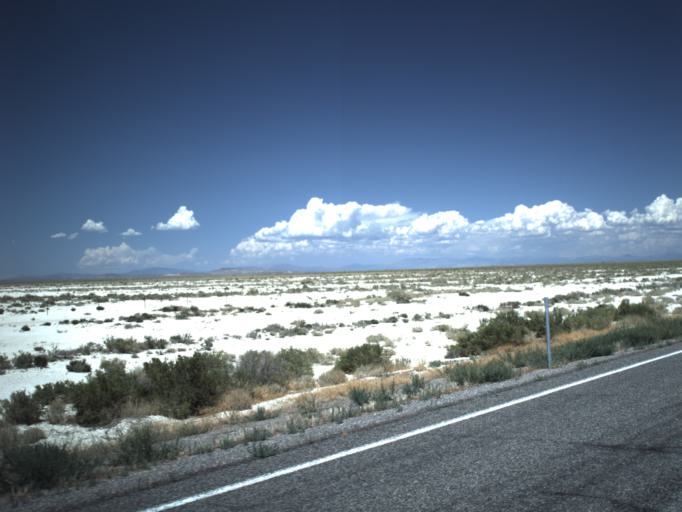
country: US
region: Utah
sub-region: Millard County
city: Delta
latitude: 39.2534
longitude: -112.8921
